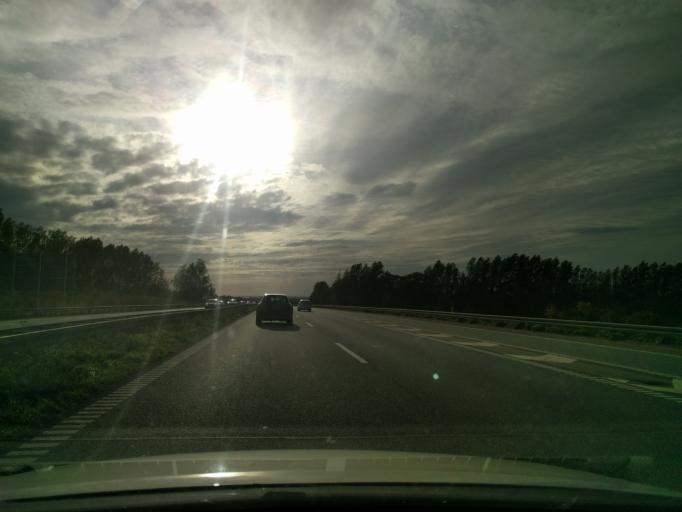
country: DK
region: Zealand
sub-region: Slagelse Kommune
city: Forlev
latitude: 55.3803
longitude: 11.3214
